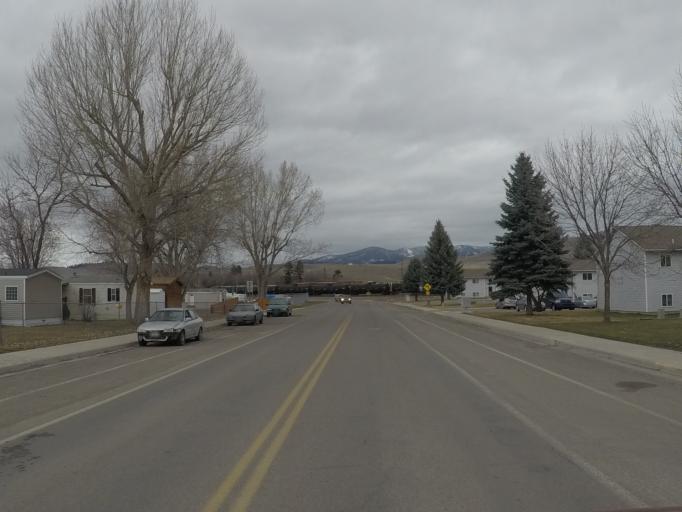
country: US
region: Montana
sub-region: Missoula County
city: Missoula
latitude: 46.8869
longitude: -114.0184
